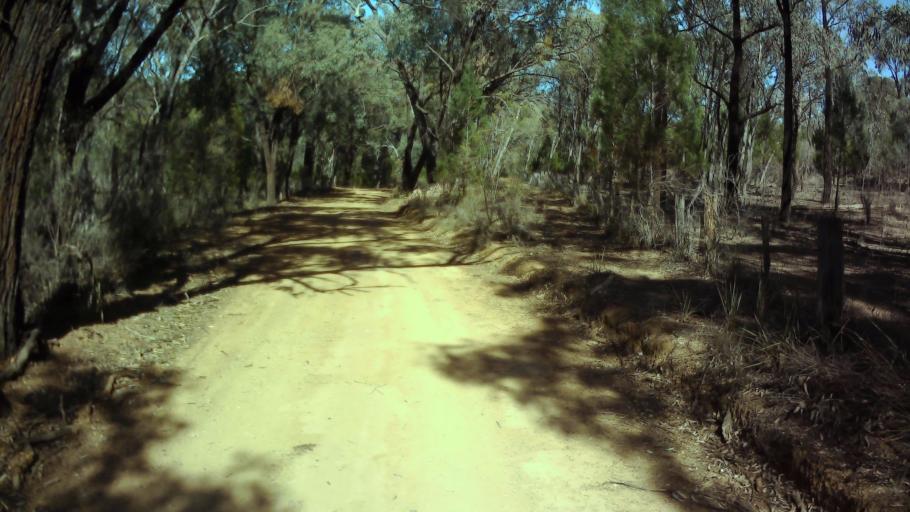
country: AU
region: New South Wales
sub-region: Weddin
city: Grenfell
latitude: -33.8992
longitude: 148.0125
